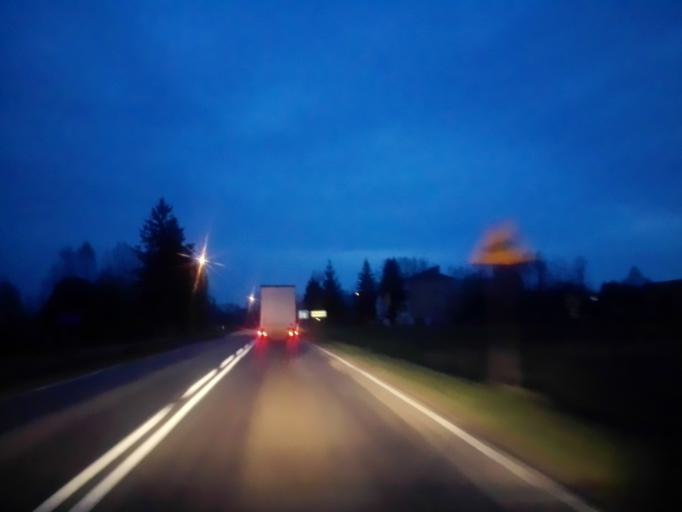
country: PL
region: Podlasie
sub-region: Powiat lomzynski
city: Sniadowo
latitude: 53.0477
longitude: 21.9921
